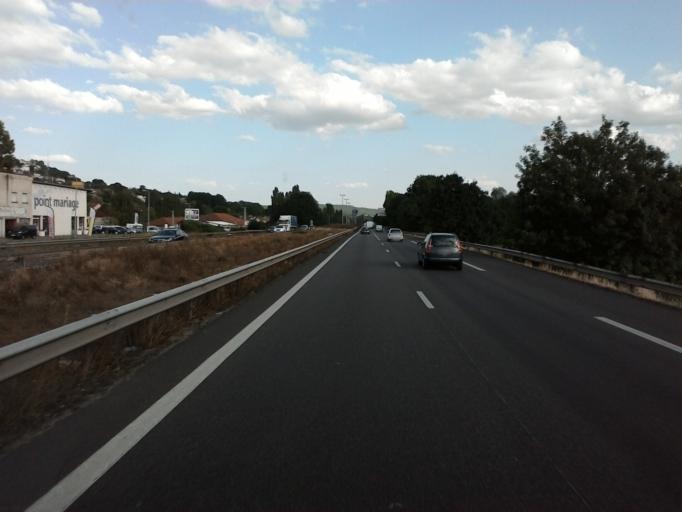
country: FR
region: Lorraine
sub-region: Departement de Meurthe-et-Moselle
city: Frouard
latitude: 48.7591
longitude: 6.1503
